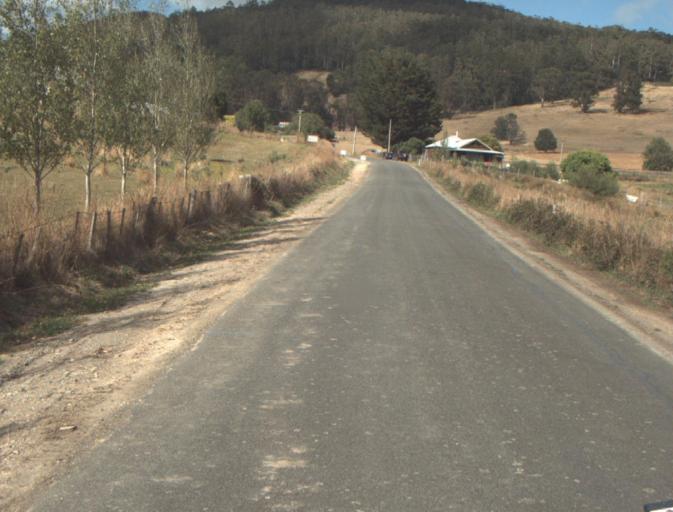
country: AU
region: Tasmania
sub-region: Launceston
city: Mayfield
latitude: -41.2580
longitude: 147.2082
